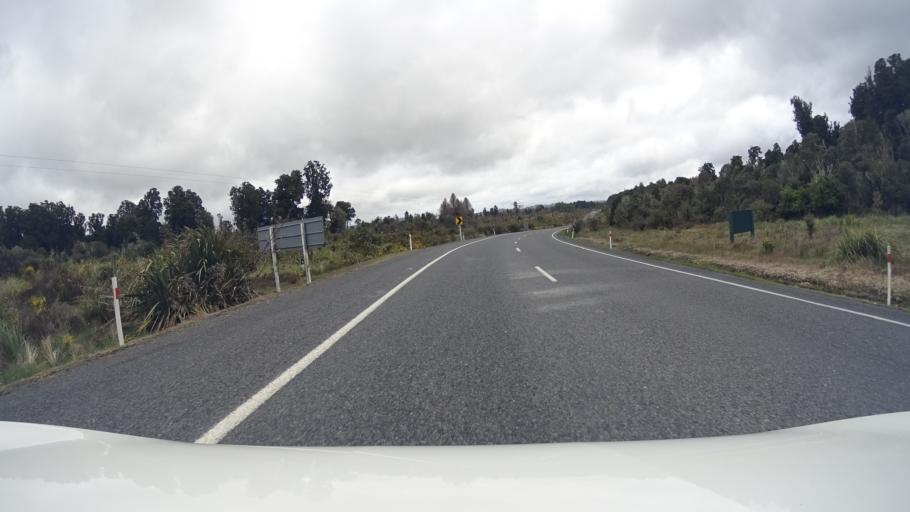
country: NZ
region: Manawatu-Wanganui
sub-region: Ruapehu District
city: Waiouru
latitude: -39.2633
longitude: 175.3901
